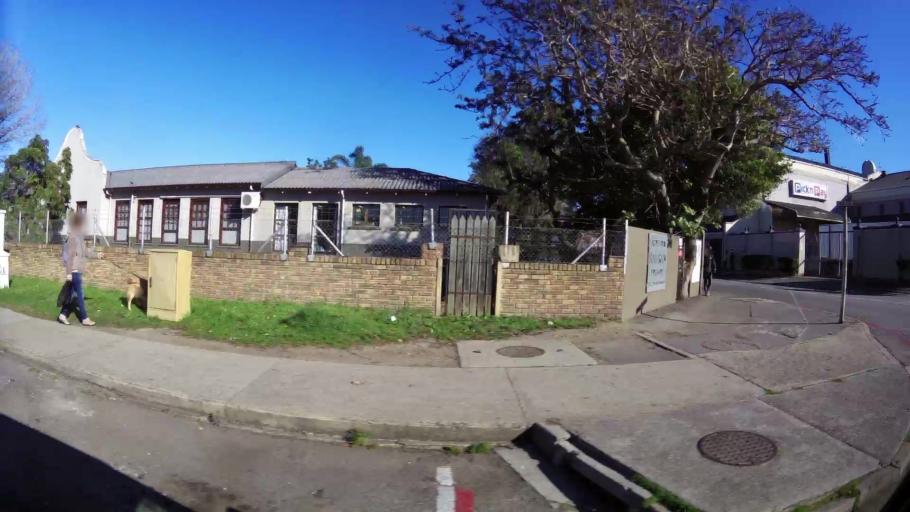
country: ZA
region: Western Cape
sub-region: Eden District Municipality
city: Knysna
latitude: -34.0377
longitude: 23.0489
